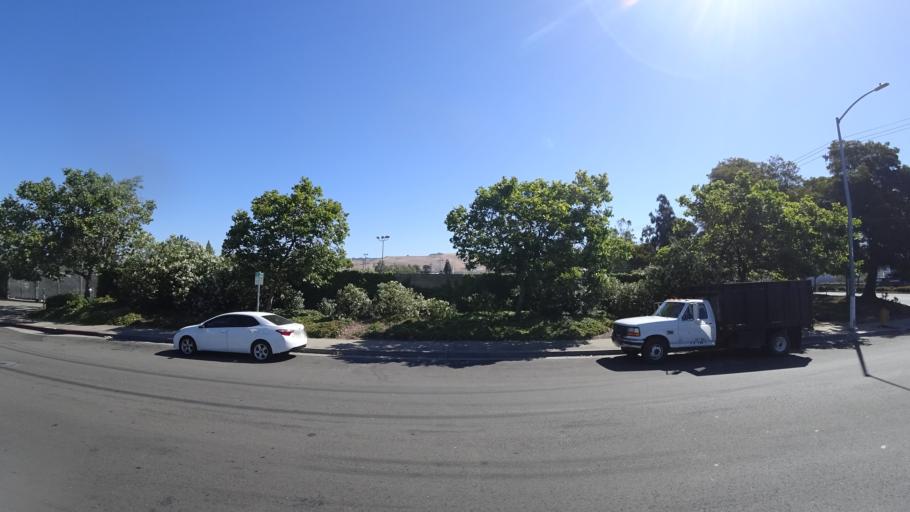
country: US
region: California
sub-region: Alameda County
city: Union City
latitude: 37.6164
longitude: -122.0644
